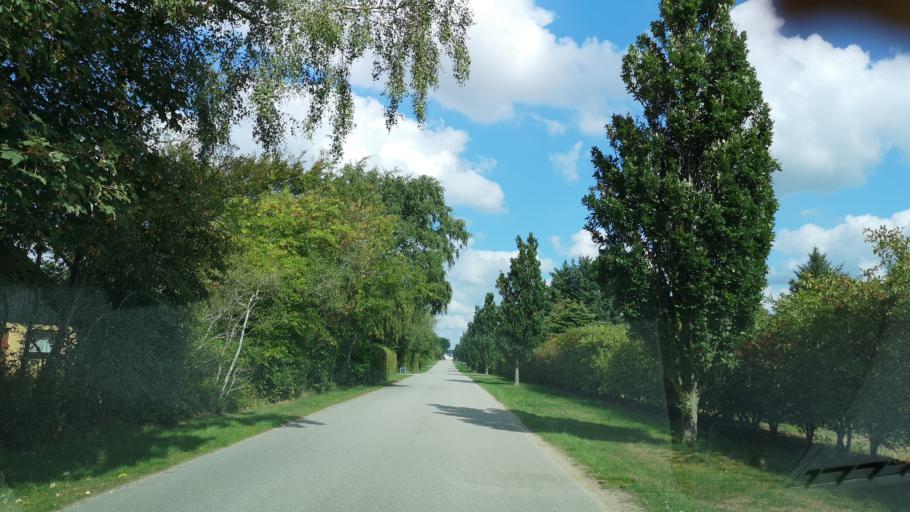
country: DK
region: Central Jutland
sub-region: Ringkobing-Skjern Kommune
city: Skjern
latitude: 55.8876
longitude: 8.3588
